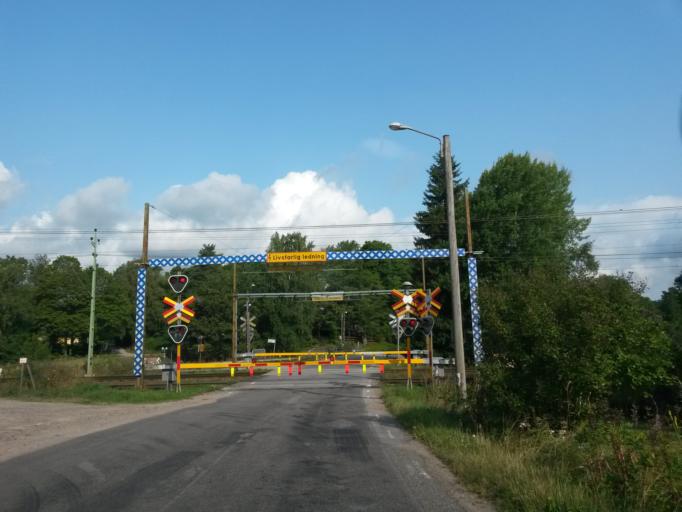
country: SE
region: Vaestra Goetaland
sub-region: Vargarda Kommun
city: Jonstorp
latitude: 58.0084
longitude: 12.7082
